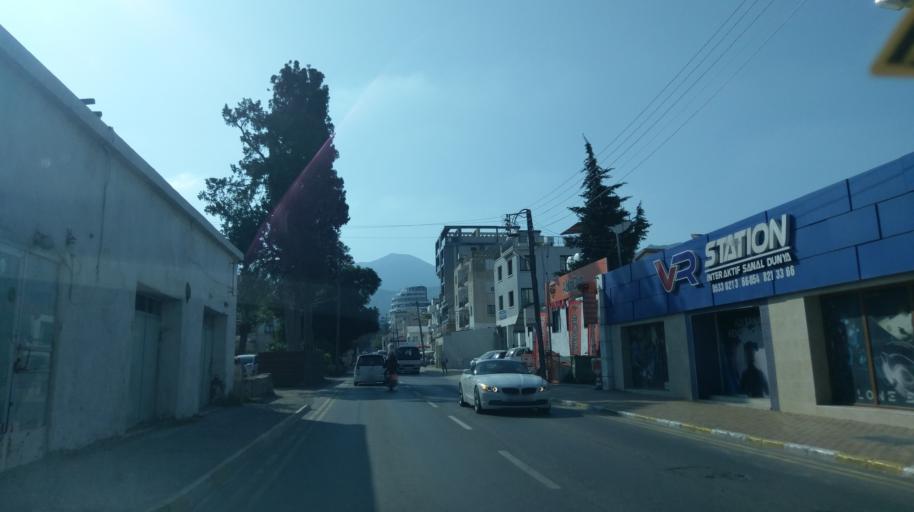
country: CY
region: Keryneia
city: Kyrenia
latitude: 35.3374
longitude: 33.3202
